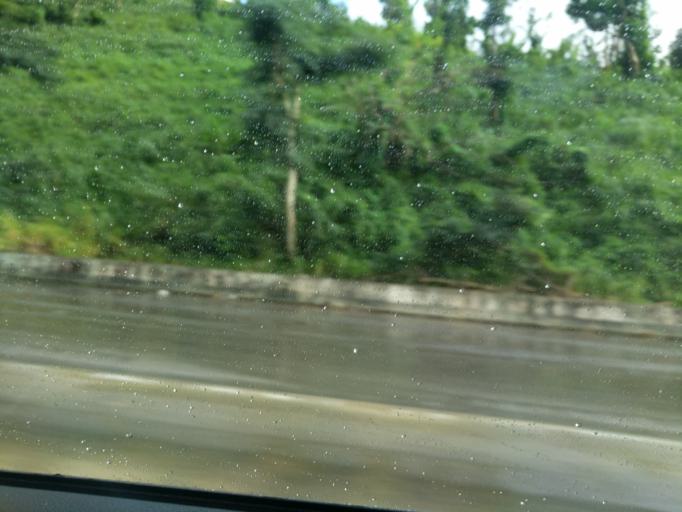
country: PR
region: Cidra
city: Bayamon
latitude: 18.1656
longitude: -66.0816
